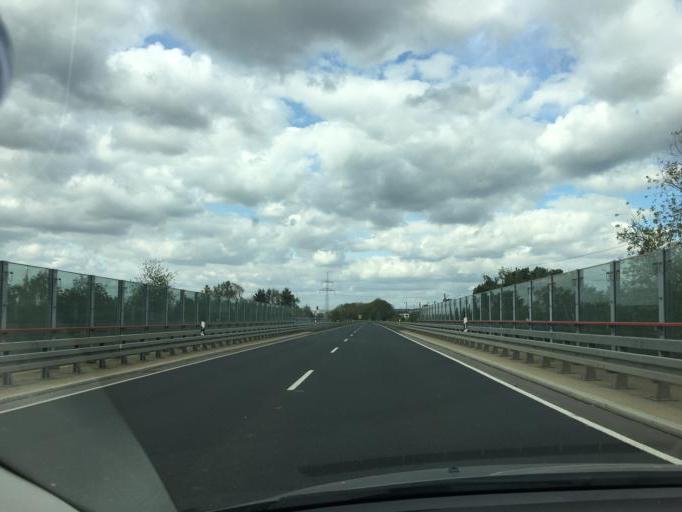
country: DE
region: Saxony
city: Coswig
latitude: 51.0990
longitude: 13.6038
